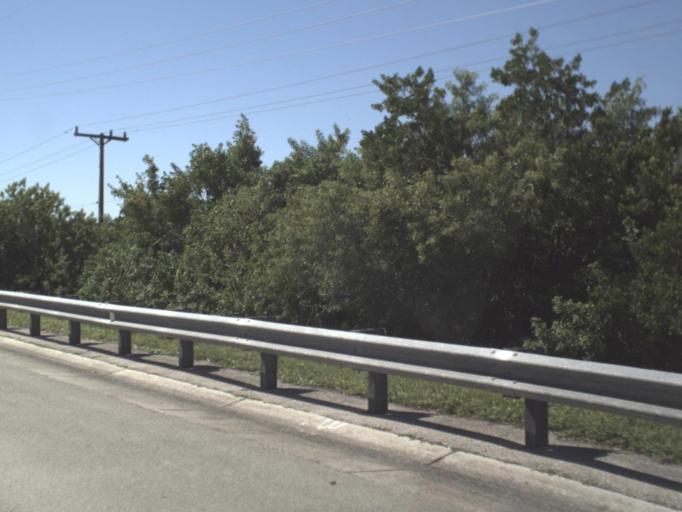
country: US
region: Florida
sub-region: Collier County
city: Marco
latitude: 25.9960
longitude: -81.7020
